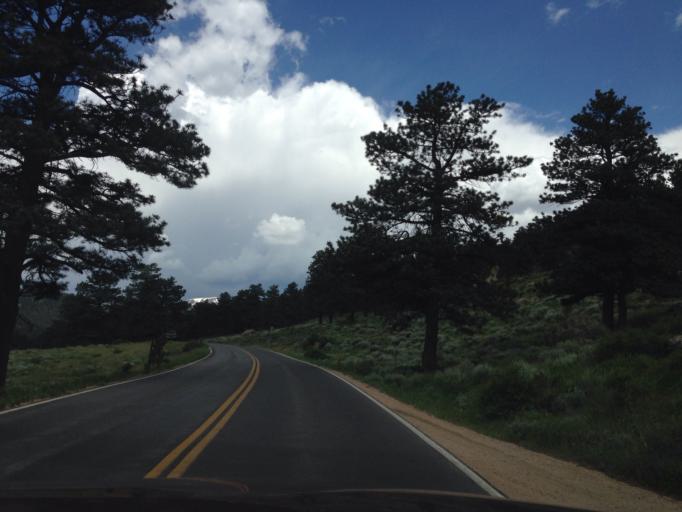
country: US
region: Colorado
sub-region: Larimer County
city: Estes Park
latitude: 40.3739
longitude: -105.5926
